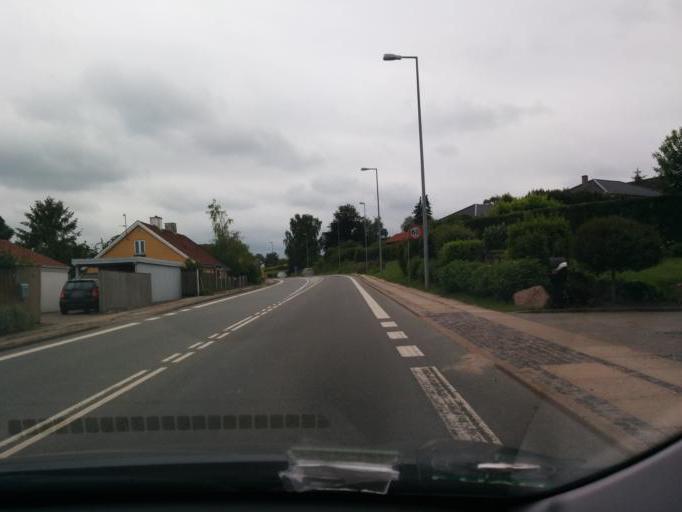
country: DK
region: Central Jutland
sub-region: Syddjurs Kommune
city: Hornslet
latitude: 56.3000
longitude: 10.3635
